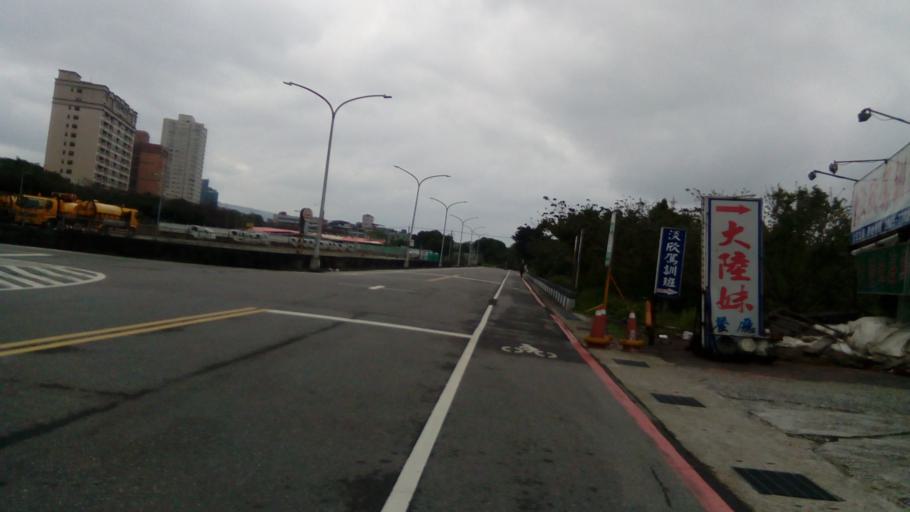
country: TW
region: Taipei
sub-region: Taipei
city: Banqiao
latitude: 25.1803
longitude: 121.4197
